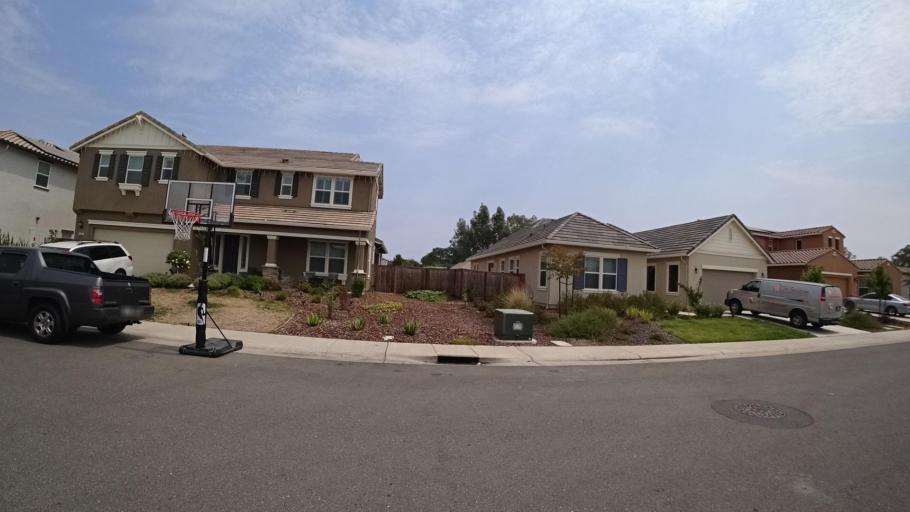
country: US
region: California
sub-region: Placer County
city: Loomis
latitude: 38.8063
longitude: -121.1973
